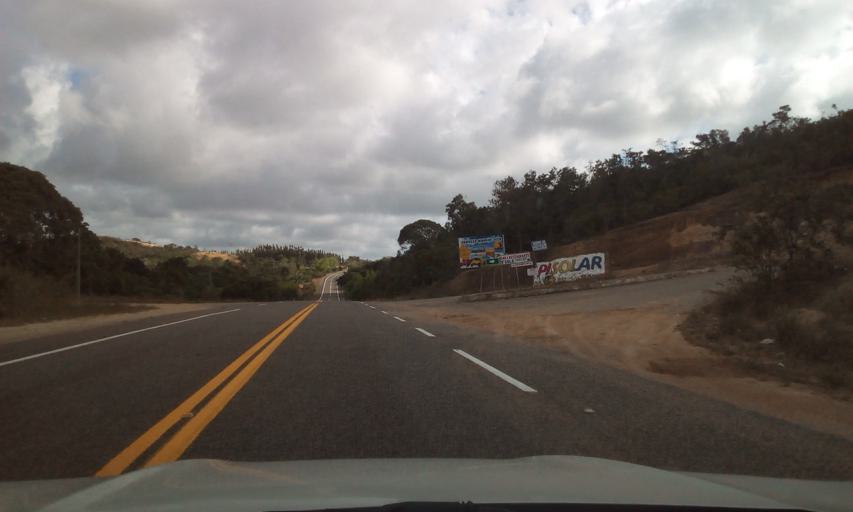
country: BR
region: Bahia
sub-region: Conde
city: Conde
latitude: -11.6709
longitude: -37.5606
